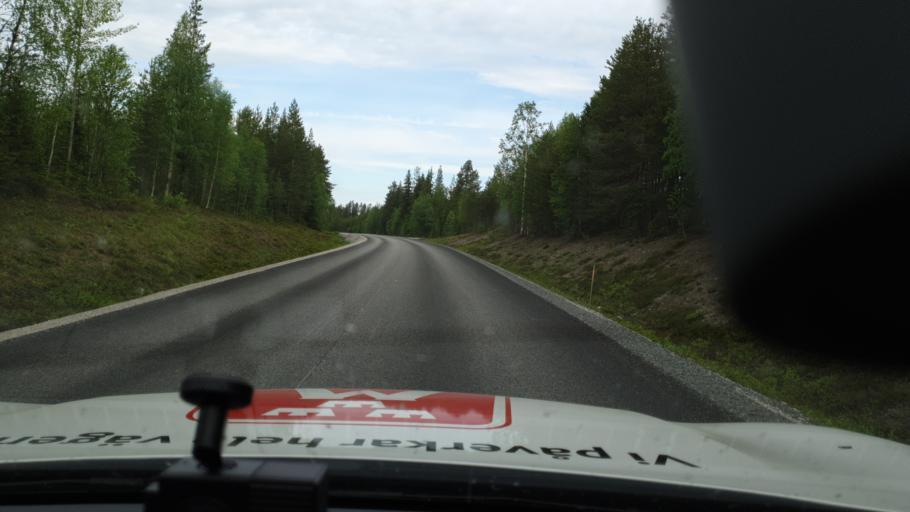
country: SE
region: Vaesterbotten
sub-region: Mala Kommun
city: Mala
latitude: 64.9803
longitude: 18.5600
